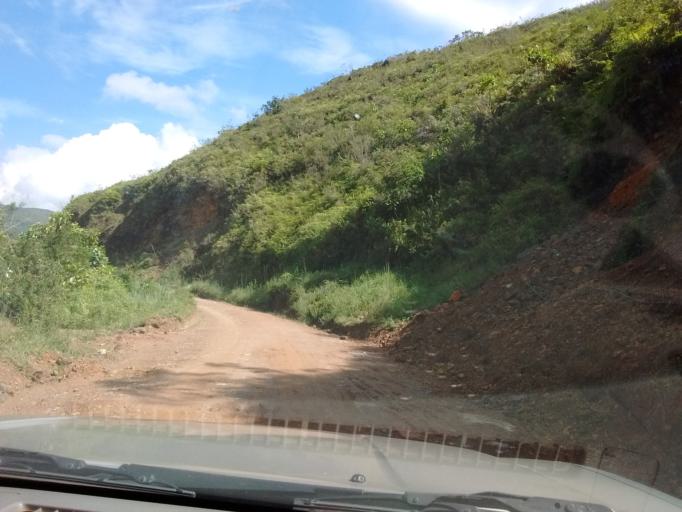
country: CO
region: Cauca
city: Morales
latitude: 2.6956
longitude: -76.7462
